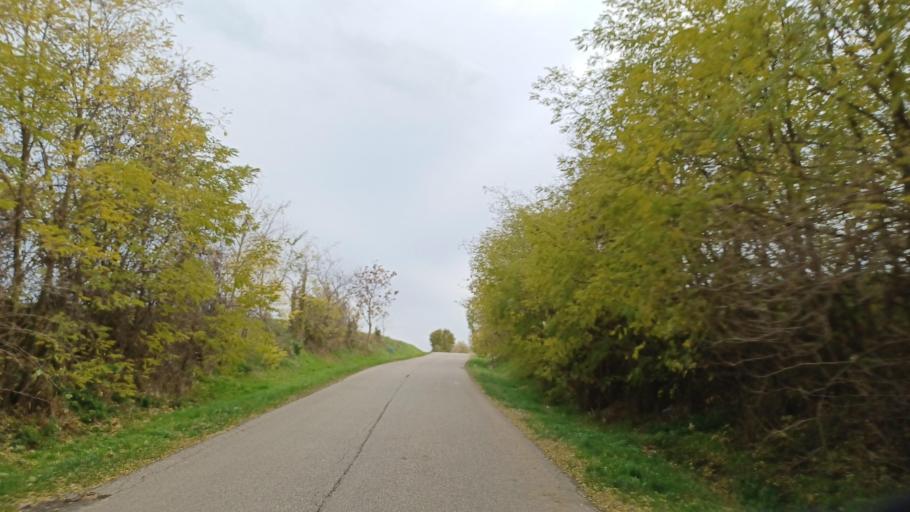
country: HU
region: Tolna
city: Nagydorog
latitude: 46.6412
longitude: 18.6066
